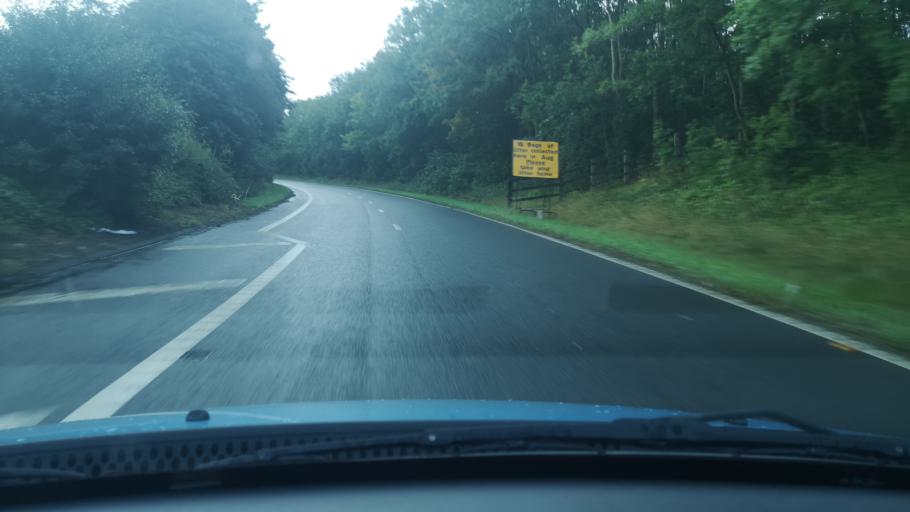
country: GB
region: England
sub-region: City and Borough of Wakefield
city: Knottingley
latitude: 53.6959
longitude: -1.2650
